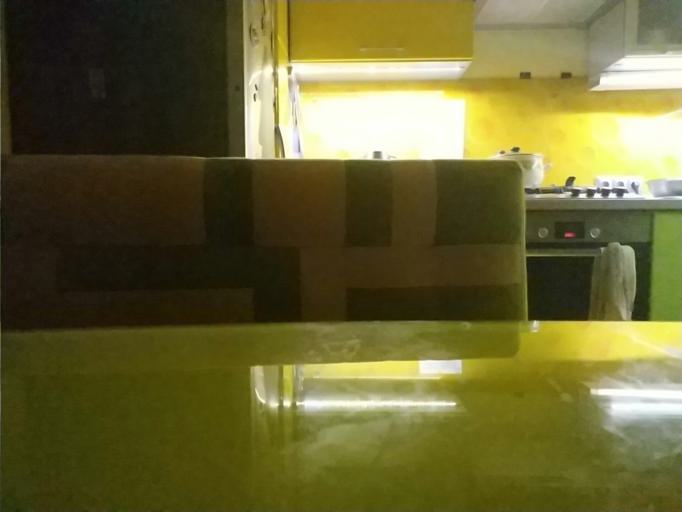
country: RU
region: Republic of Karelia
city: Pyaozerskiy
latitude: 65.8675
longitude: 30.4421
